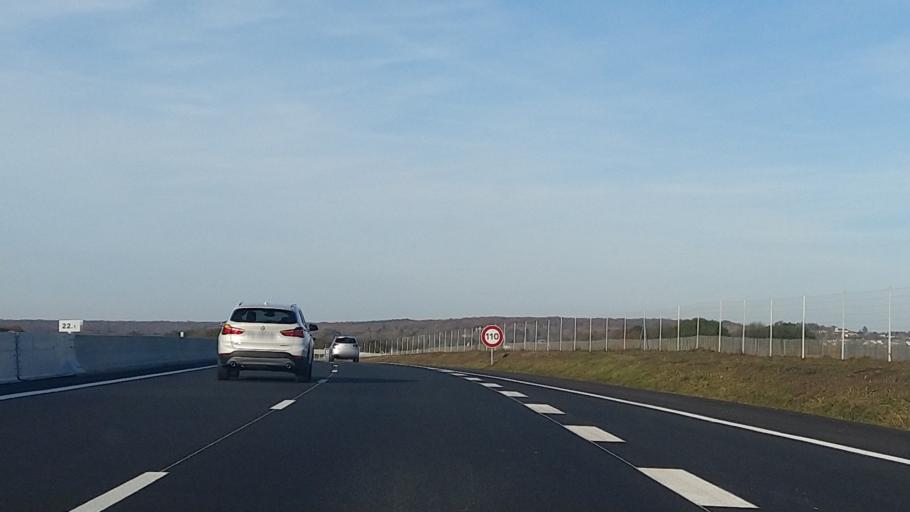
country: FR
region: Ile-de-France
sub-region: Departement du Val-d'Oise
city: Montsoult
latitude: 49.0743
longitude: 2.3330
